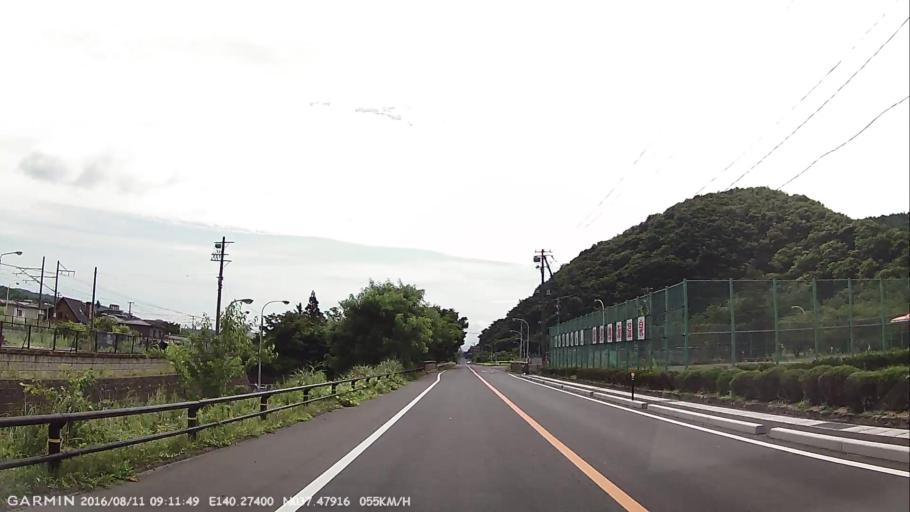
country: JP
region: Fukushima
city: Motomiya
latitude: 37.4791
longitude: 140.2742
